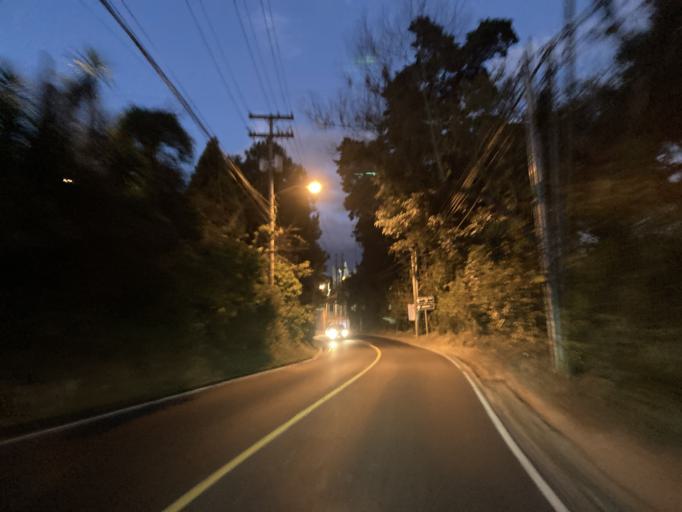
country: GT
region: Guatemala
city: Santa Catarina Pinula
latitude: 14.6012
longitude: -90.4669
